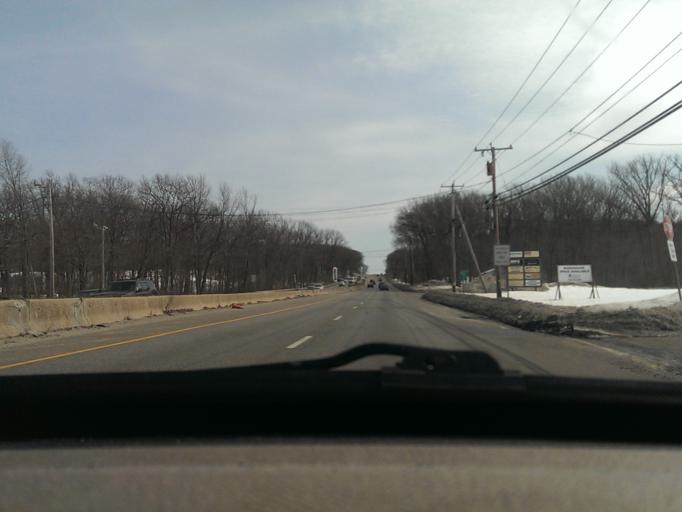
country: US
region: Massachusetts
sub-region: Worcester County
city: Millbury
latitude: 42.1766
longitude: -71.7575
